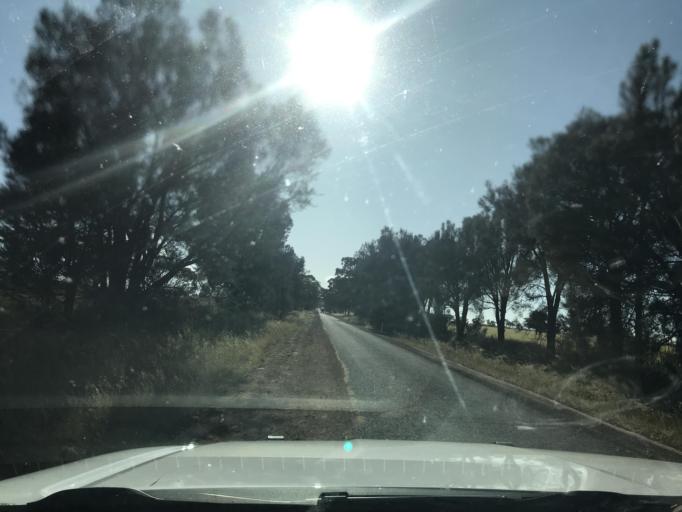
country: AU
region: Victoria
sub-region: Horsham
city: Horsham
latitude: -36.6913
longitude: 141.5374
